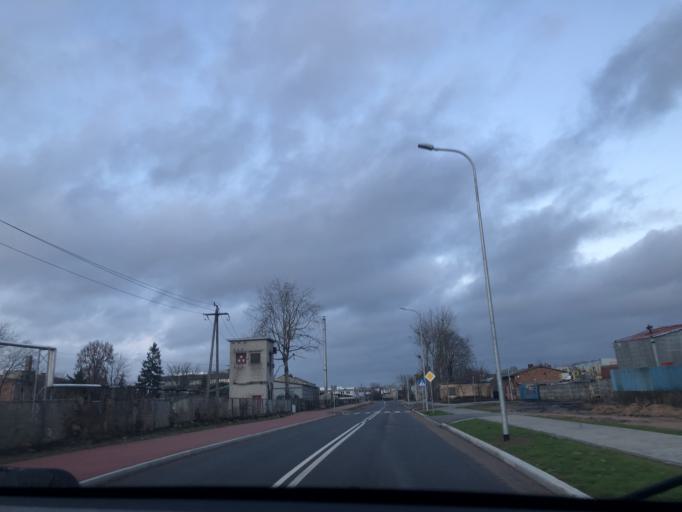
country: PL
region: Podlasie
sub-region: Lomza
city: Lomza
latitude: 53.1722
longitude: 22.0622
